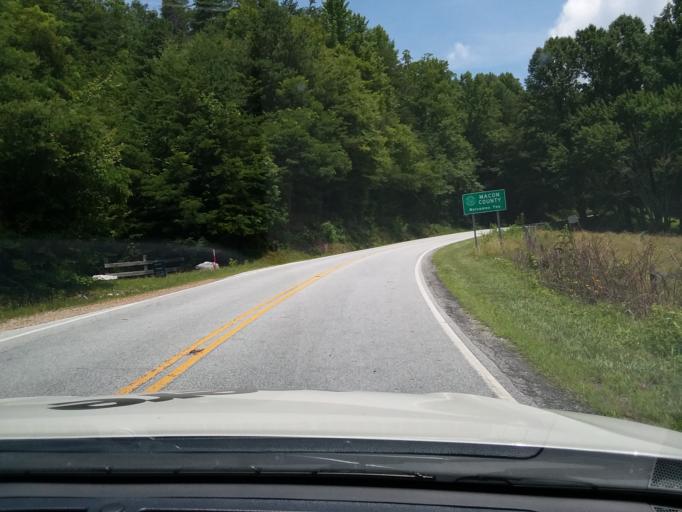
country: US
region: Georgia
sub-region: Rabun County
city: Mountain City
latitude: 35.0022
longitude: -83.3363
